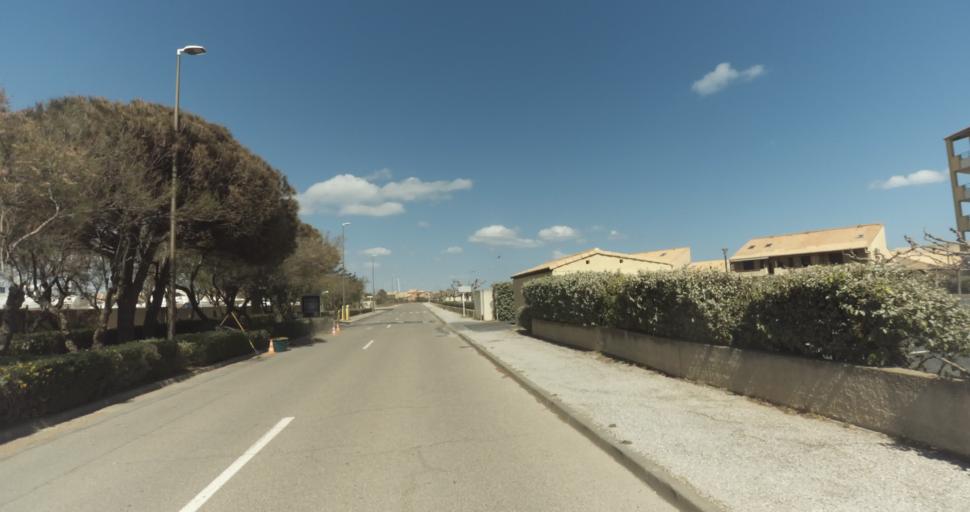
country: FR
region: Languedoc-Roussillon
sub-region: Departement de l'Aude
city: Leucate
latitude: 42.8662
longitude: 3.0440
